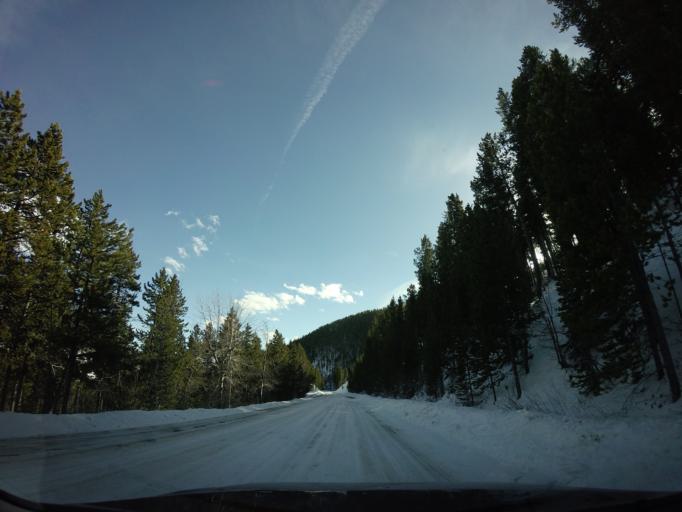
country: US
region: Montana
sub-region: Carbon County
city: Red Lodge
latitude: 45.1870
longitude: -109.3317
